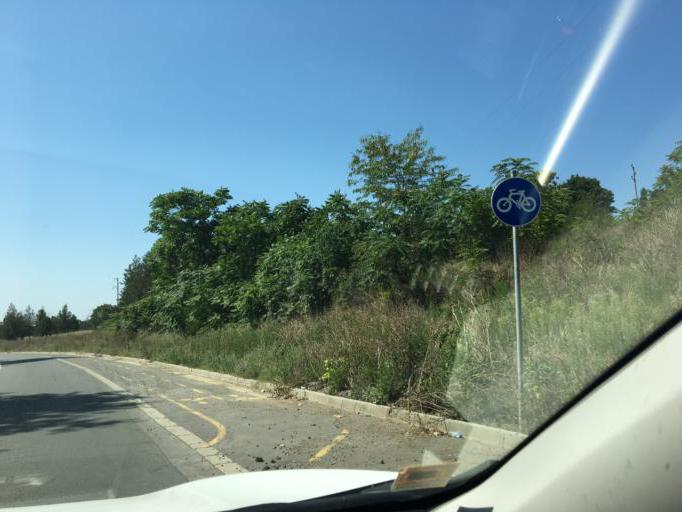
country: BG
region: Burgas
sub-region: Obshtina Kameno
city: Kameno
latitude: 42.6190
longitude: 27.3946
